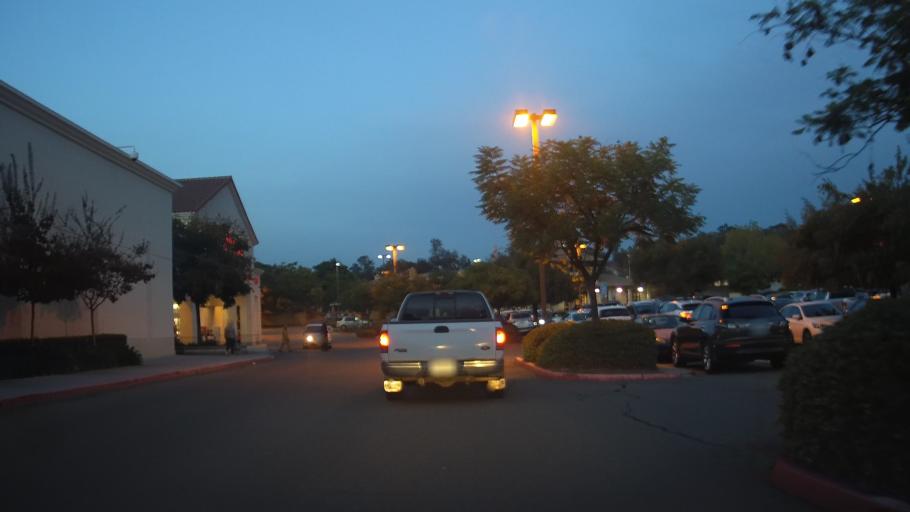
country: US
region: California
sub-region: San Diego County
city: Rancho San Diego
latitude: 32.7468
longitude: -116.9285
